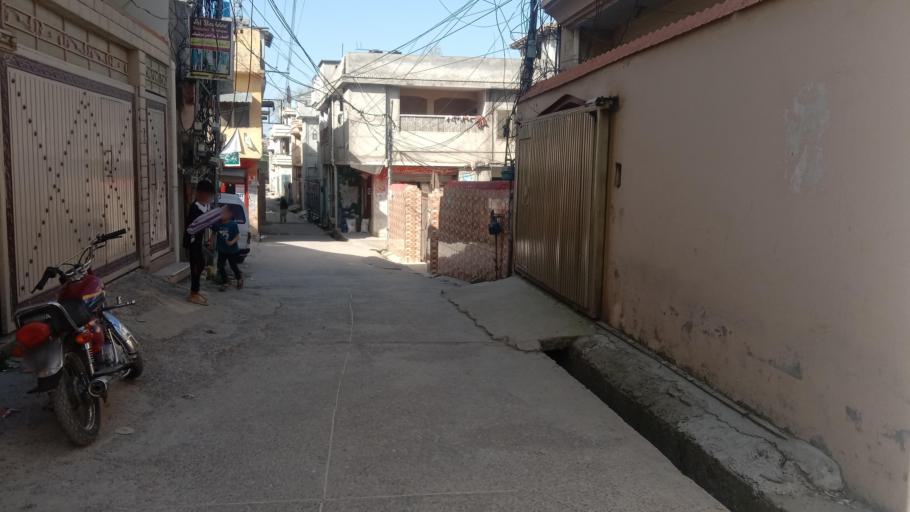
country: PK
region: Khyber Pakhtunkhwa
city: Abbottabad
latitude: 34.1770
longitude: 73.2251
